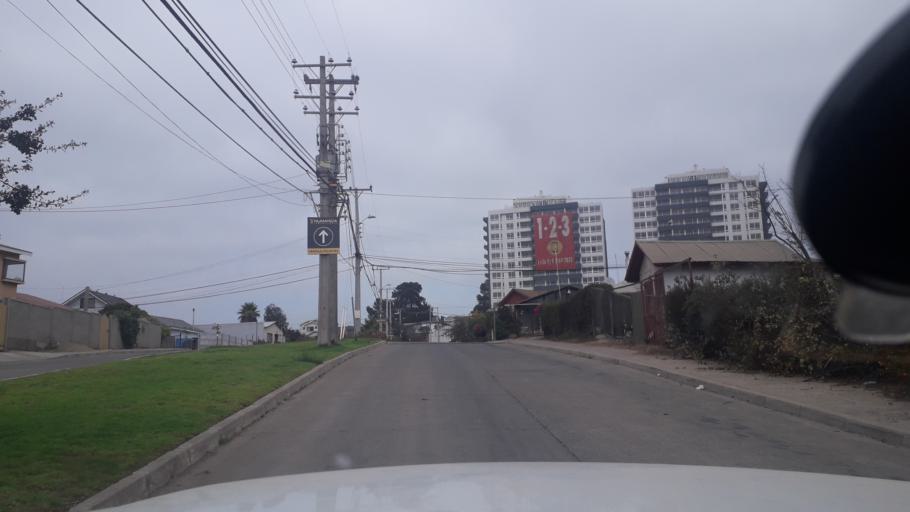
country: CL
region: Valparaiso
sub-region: Provincia de Valparaiso
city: Vina del Mar
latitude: -32.9365
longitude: -71.5297
